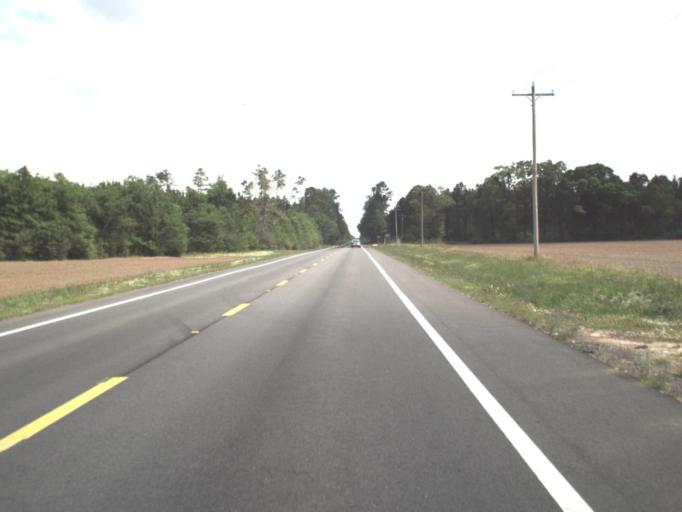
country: US
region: Florida
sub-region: Escambia County
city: Century
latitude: 30.8538
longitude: -87.1506
